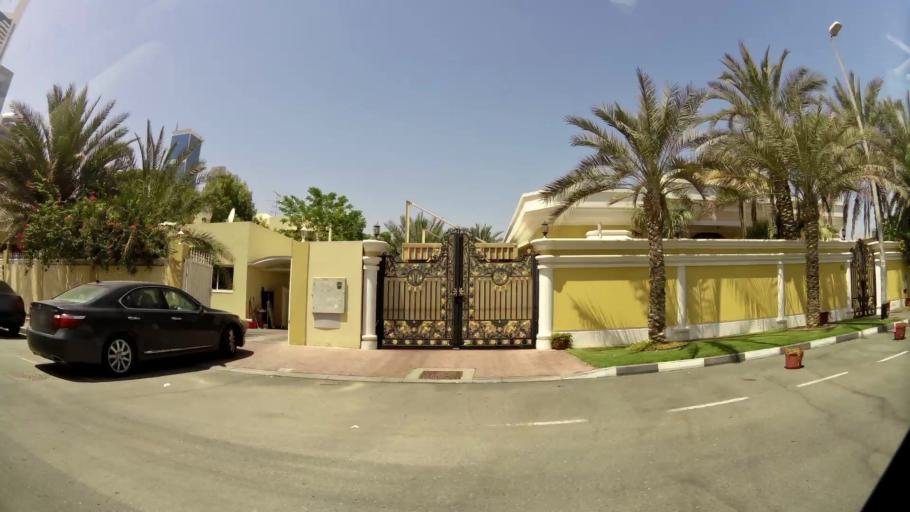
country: AE
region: Dubai
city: Dubai
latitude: 25.2141
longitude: 55.2720
